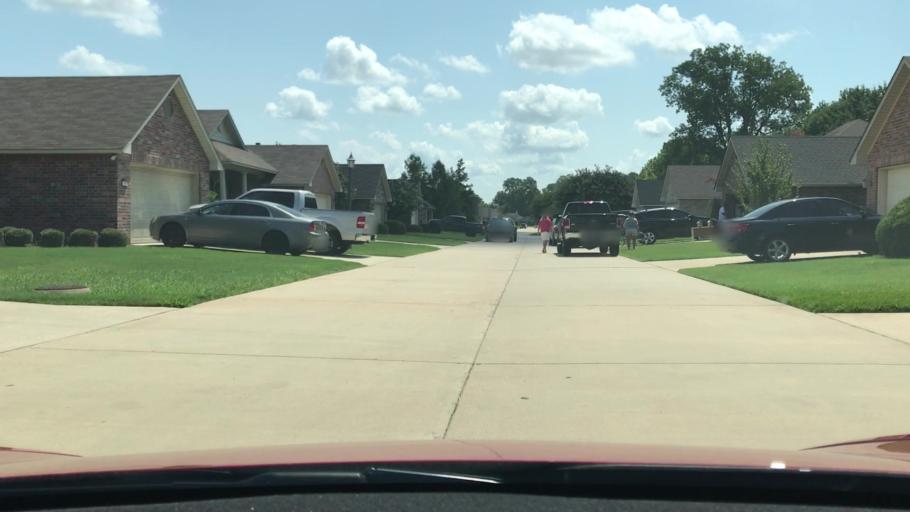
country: US
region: Louisiana
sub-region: Bossier Parish
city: Bossier City
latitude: 32.4135
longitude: -93.6903
